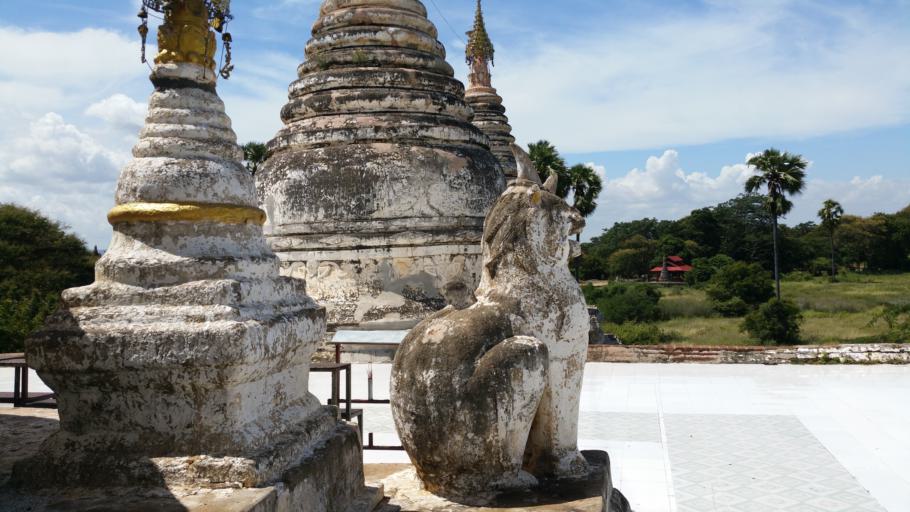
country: MM
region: Magway
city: Pakokku
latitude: 21.1741
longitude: 94.8692
